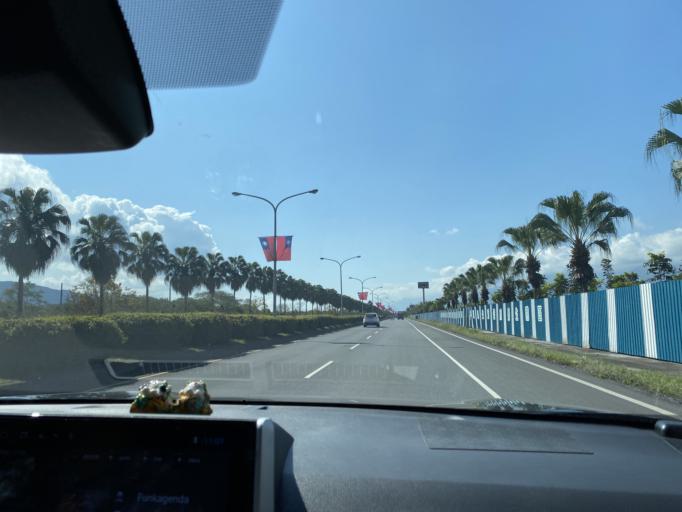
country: TW
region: Taiwan
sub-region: Hualien
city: Hualian
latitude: 23.8678
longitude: 121.5333
